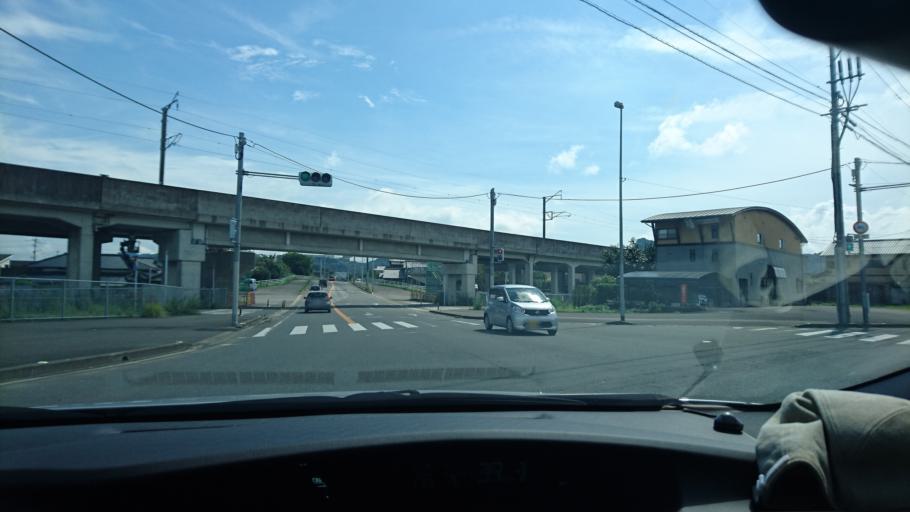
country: JP
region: Saga Prefecture
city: Takeocho-takeo
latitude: 33.2006
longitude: 130.0293
